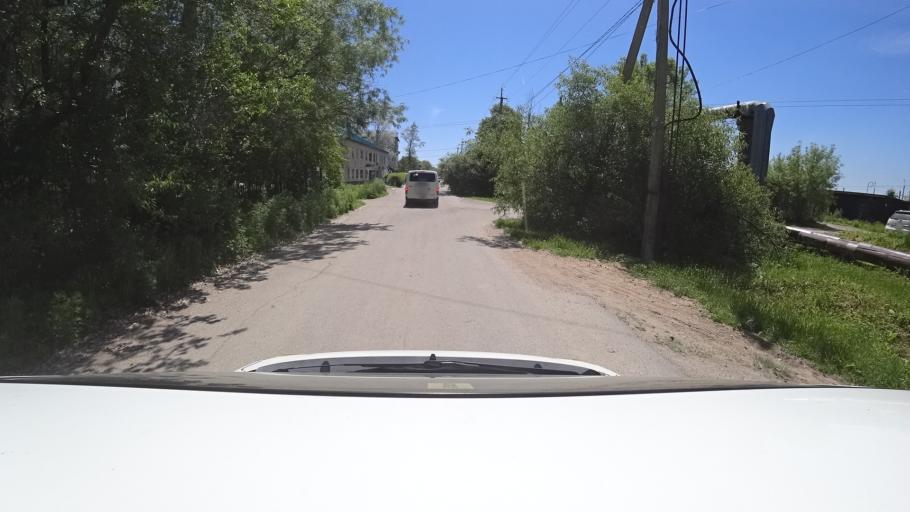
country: RU
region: Khabarovsk Krai
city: Topolevo
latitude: 48.5060
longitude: 135.1687
